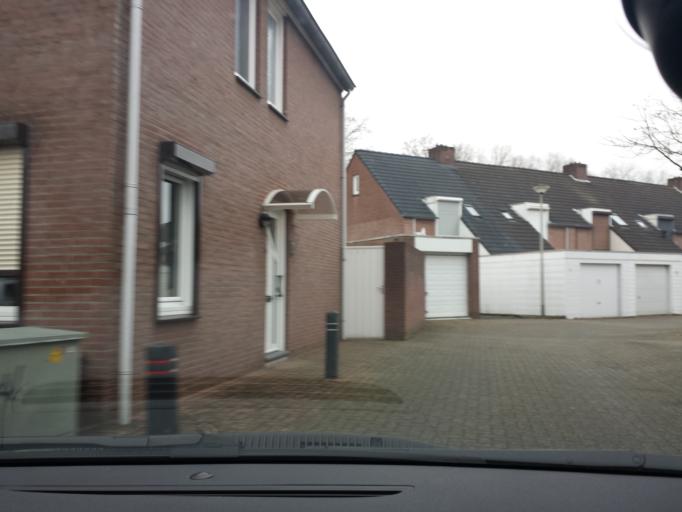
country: NL
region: Limburg
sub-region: Gemeente Kerkrade
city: Kerkrade
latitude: 50.8944
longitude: 6.0521
